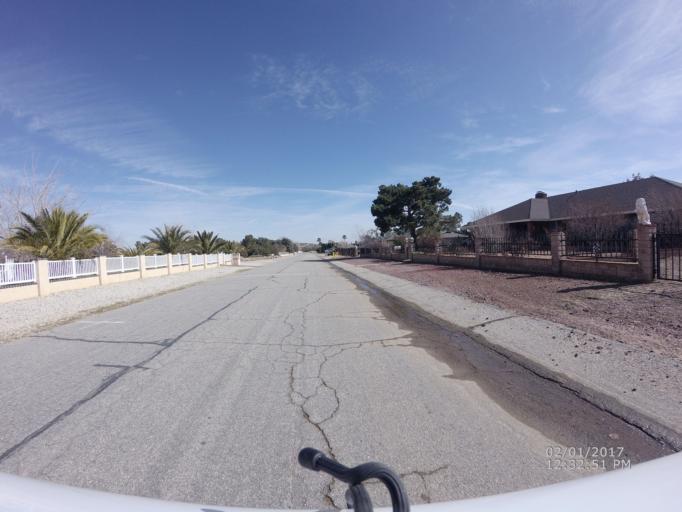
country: US
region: California
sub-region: Los Angeles County
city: Desert View Highlands
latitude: 34.5616
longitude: -118.1455
